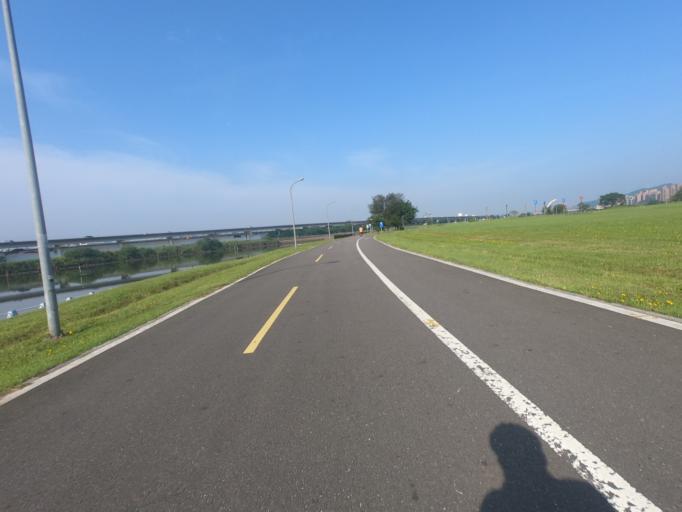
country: TW
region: Taipei
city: Taipei
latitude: 25.0738
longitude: 121.5634
